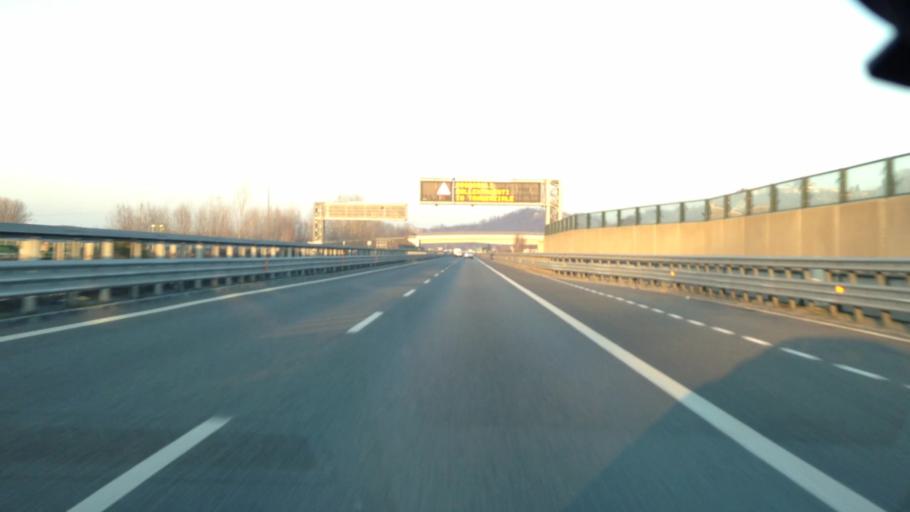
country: IT
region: Piedmont
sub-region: Provincia di Asti
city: Mongardino
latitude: 44.8514
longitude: 8.1955
